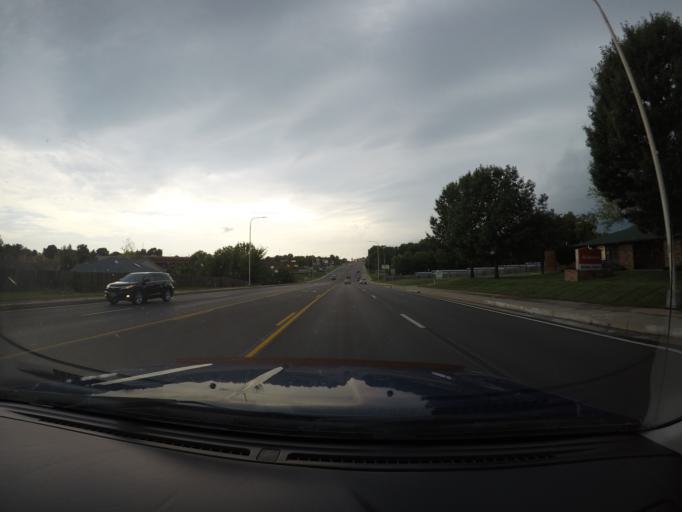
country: US
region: Missouri
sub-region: Jackson County
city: East Independence
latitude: 39.1239
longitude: -94.3632
